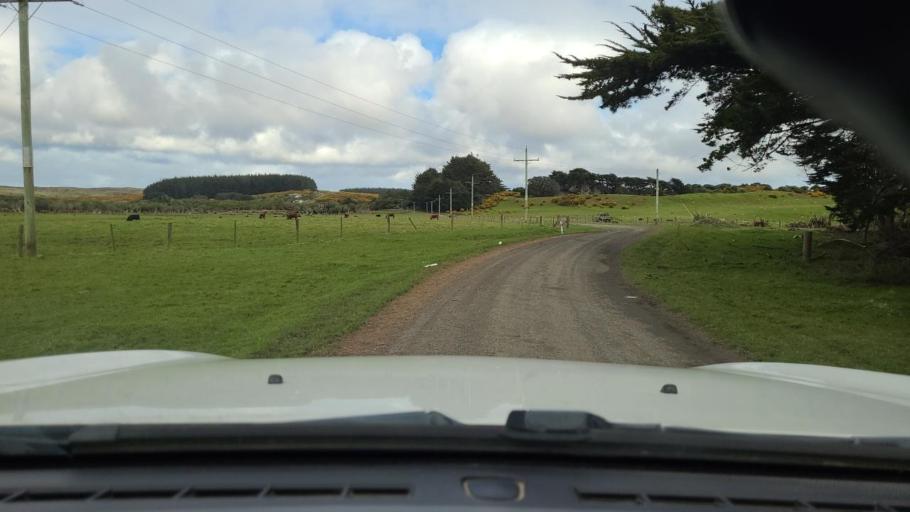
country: NZ
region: Chatham Islands
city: Waitangi
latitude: -43.9606
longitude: -176.5500
